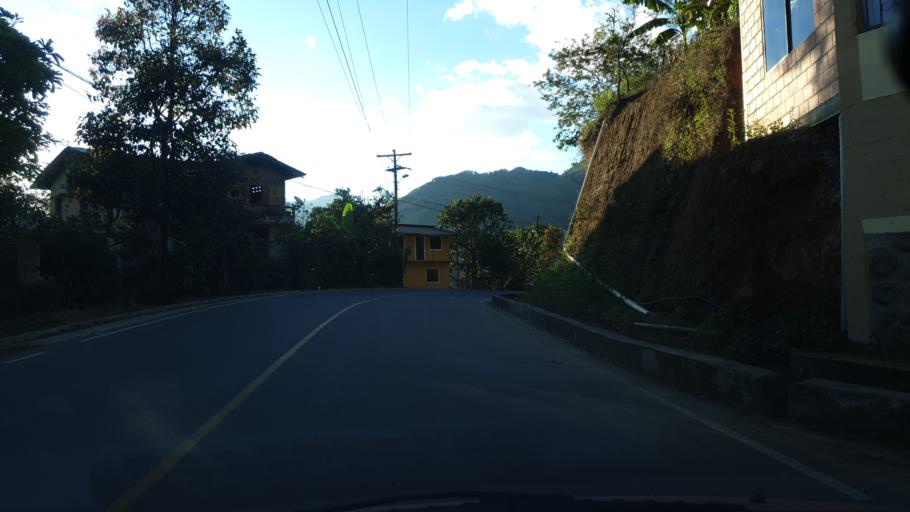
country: EC
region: El Oro
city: Zaruma
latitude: -3.6048
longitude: -79.6311
